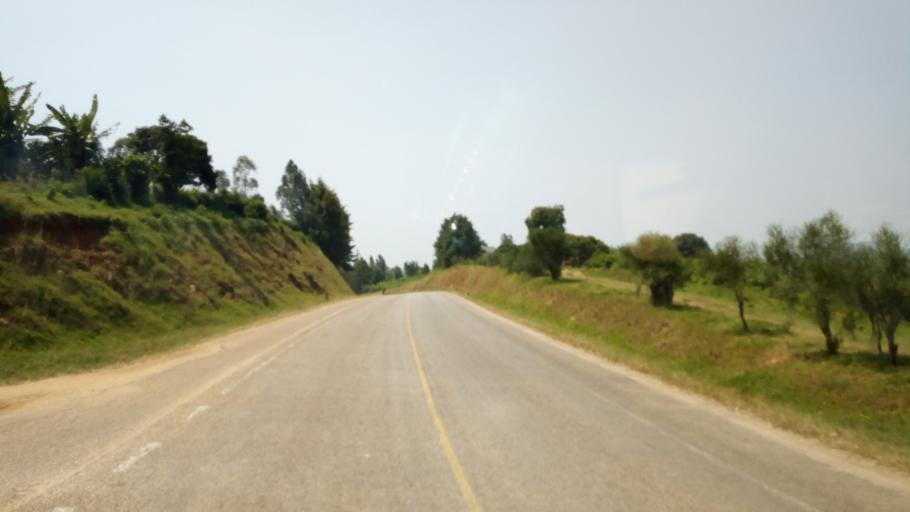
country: UG
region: Western Region
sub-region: Ntungamo District
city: Ntungamo
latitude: -0.8175
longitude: 30.1555
